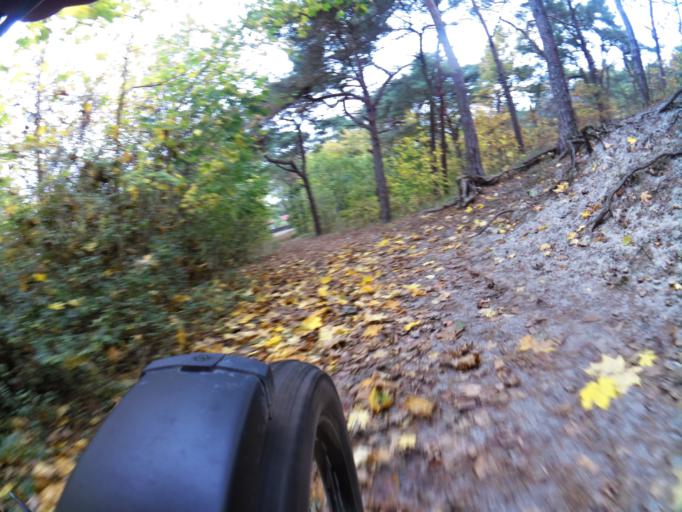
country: PL
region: Pomeranian Voivodeship
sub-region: Powiat pucki
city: Jastarnia
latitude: 54.6974
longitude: 18.6876
